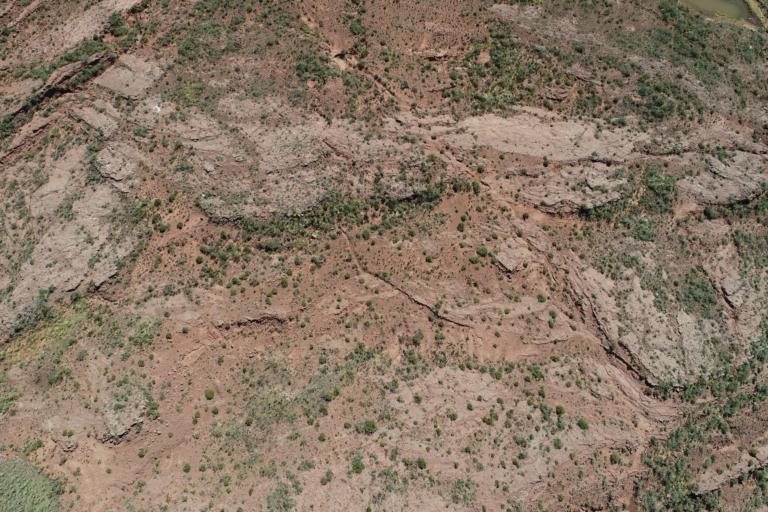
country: BO
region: La Paz
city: Tiahuanaco
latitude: -16.5974
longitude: -68.7570
